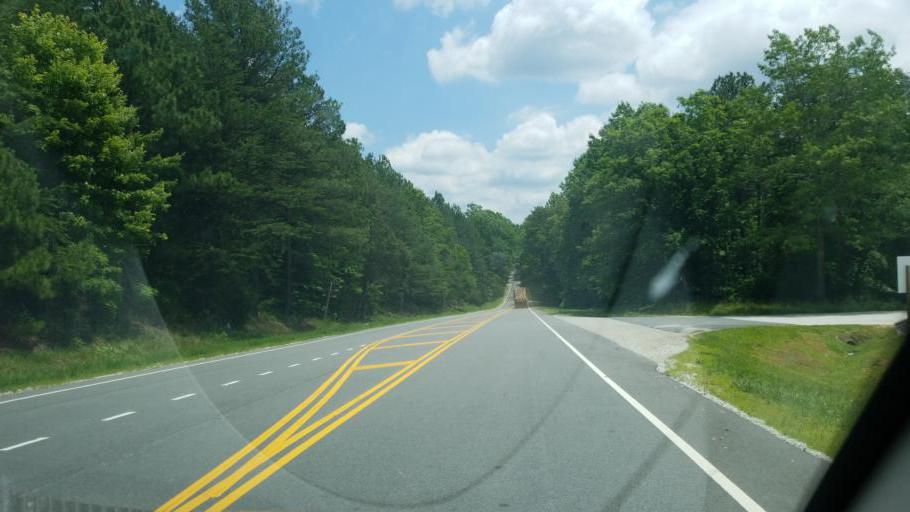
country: US
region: Virginia
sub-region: Amherst County
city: Amherst
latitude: 37.5726
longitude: -78.8960
